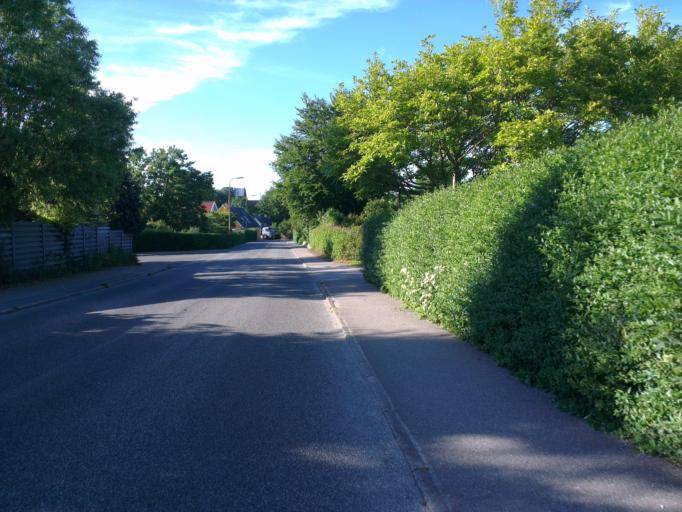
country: DK
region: Capital Region
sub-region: Frederikssund Kommune
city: Skibby
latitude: 55.7809
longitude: 12.0181
